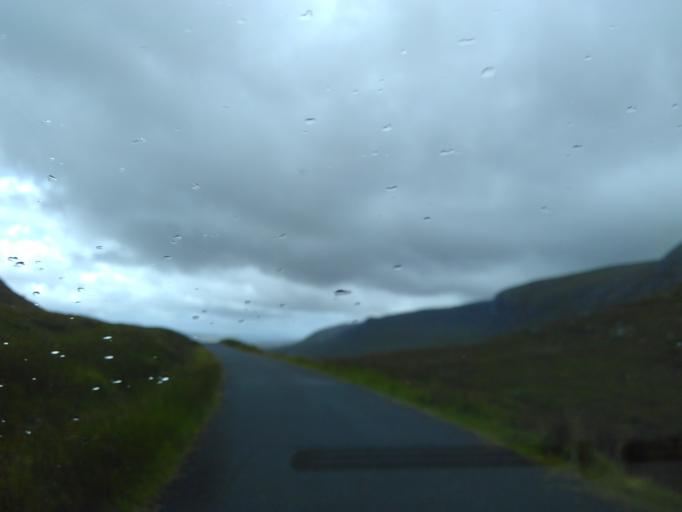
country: IE
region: Ulster
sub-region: County Donegal
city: Dunlewy
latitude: 54.9754
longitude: -8.0765
